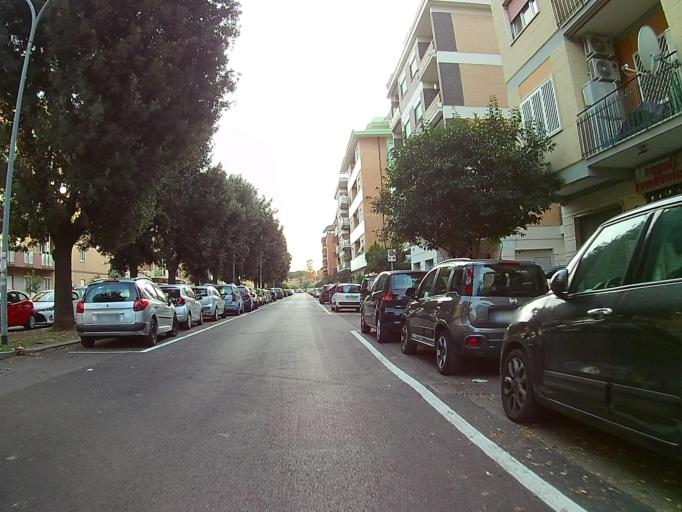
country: IT
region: Latium
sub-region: Citta metropolitana di Roma Capitale
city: Lido di Ostia
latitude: 41.7360
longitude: 12.2851
